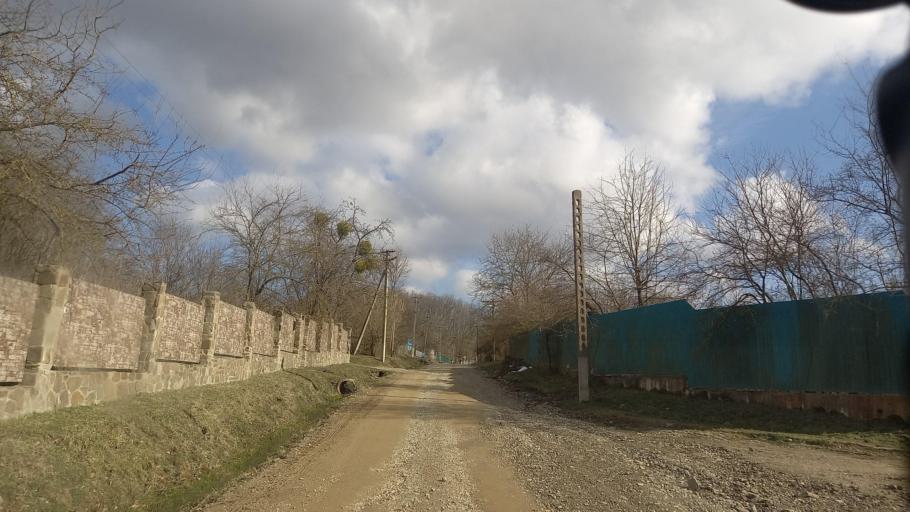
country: RU
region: Krasnodarskiy
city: Smolenskaya
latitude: 44.6045
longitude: 38.8534
